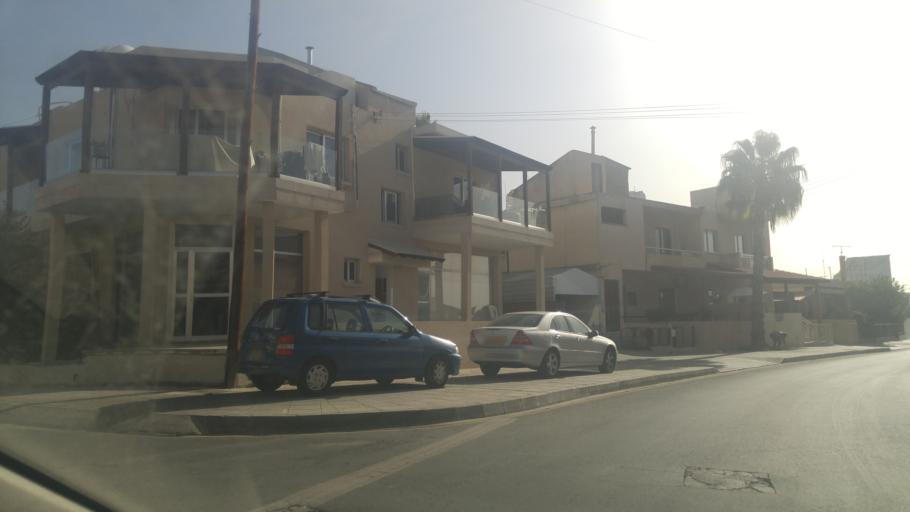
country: CY
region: Limassol
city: Pano Polemidia
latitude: 34.6924
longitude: 33.0028
